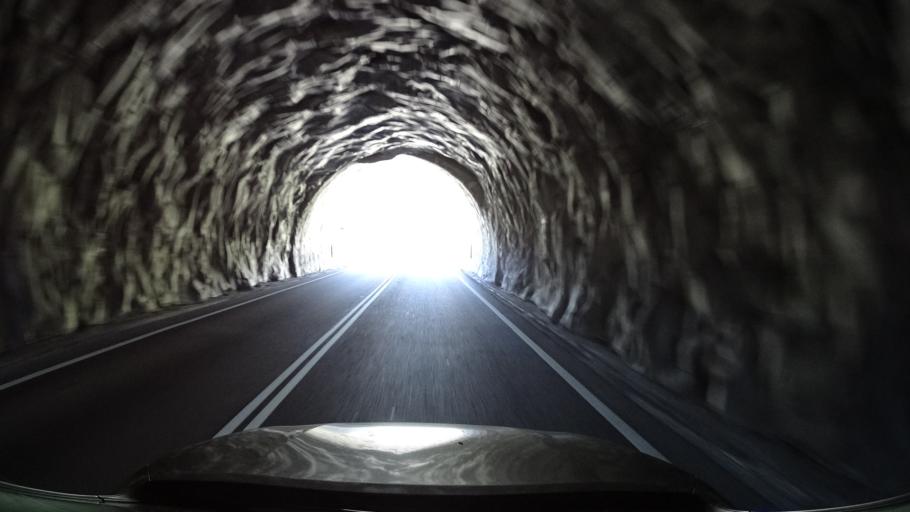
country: ES
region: Castille and Leon
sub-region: Provincia de Leon
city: La Pola de Gordon
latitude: 42.8593
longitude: -5.6745
